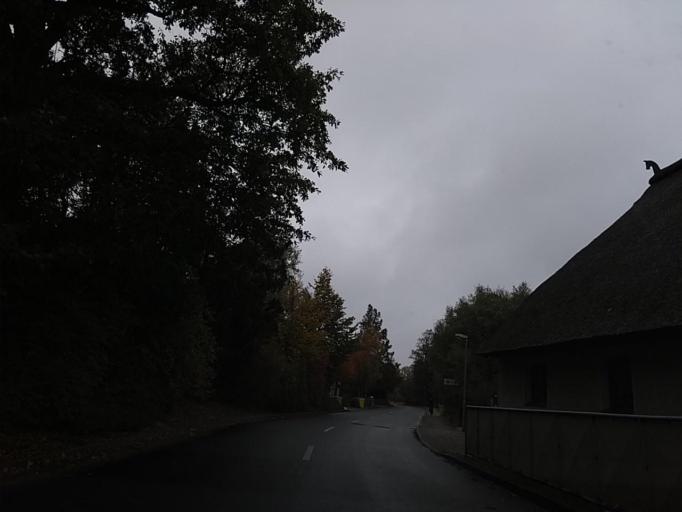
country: DE
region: Mecklenburg-Vorpommern
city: Ostseebad Kuhlungsborn
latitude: 54.1347
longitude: 11.7517
